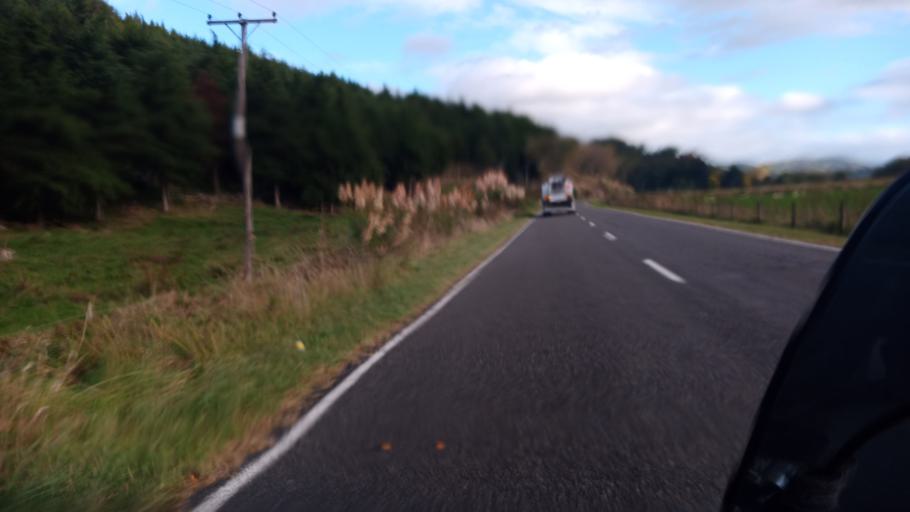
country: NZ
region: Gisborne
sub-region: Gisborne District
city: Gisborne
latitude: -38.6034
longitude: 177.8066
